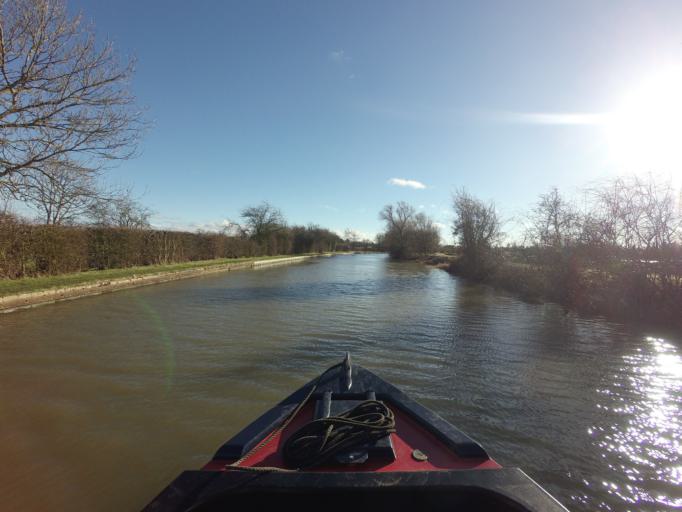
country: GB
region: England
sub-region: Northamptonshire
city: Bugbrooke
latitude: 52.2125
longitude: -1.0236
